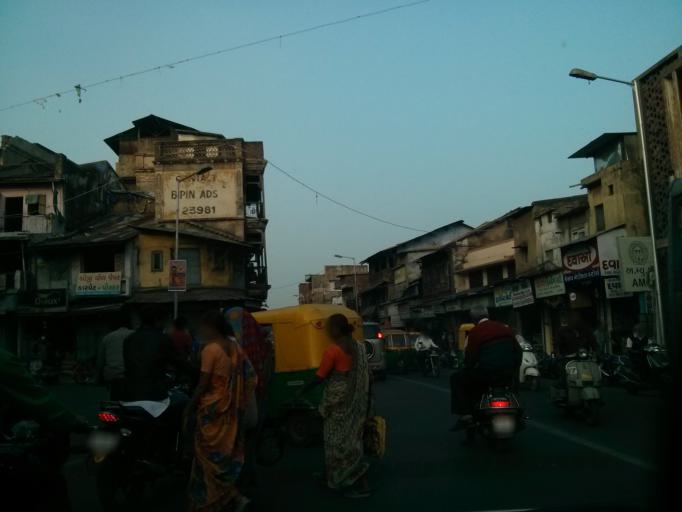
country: IN
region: Gujarat
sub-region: Ahmadabad
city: Ahmedabad
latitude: 23.0363
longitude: 72.5876
